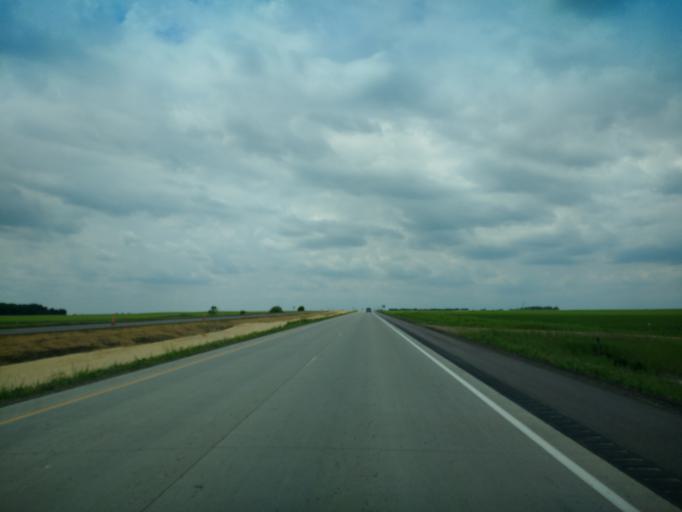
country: US
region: Minnesota
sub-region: Cottonwood County
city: Mountain Lake
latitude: 43.9208
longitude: -94.9922
